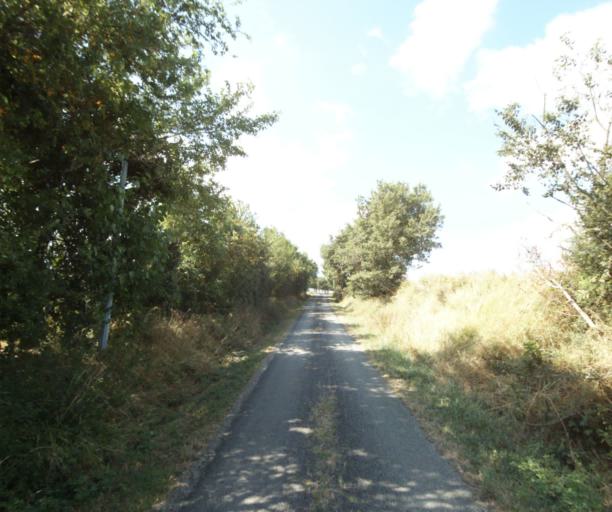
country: FR
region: Midi-Pyrenees
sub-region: Departement de la Haute-Garonne
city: Avignonet-Lauragais
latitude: 43.4361
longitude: 1.7934
